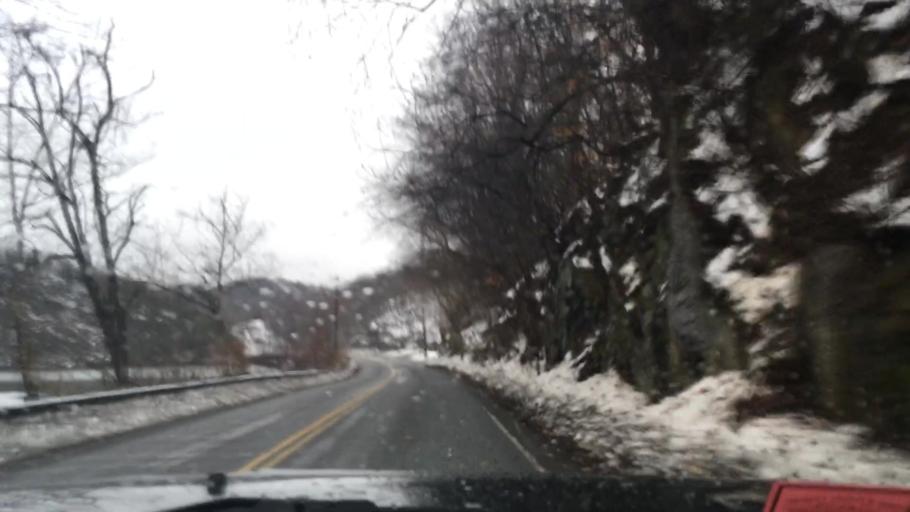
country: US
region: Virginia
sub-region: Pulaski County
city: Dublin
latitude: 37.0050
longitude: -80.6853
